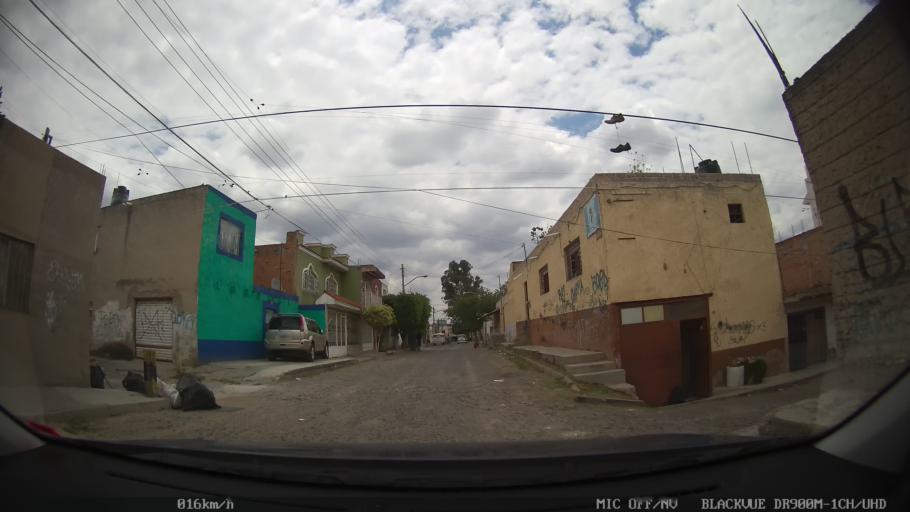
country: MX
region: Jalisco
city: Tonala
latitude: 20.6513
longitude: -103.2579
